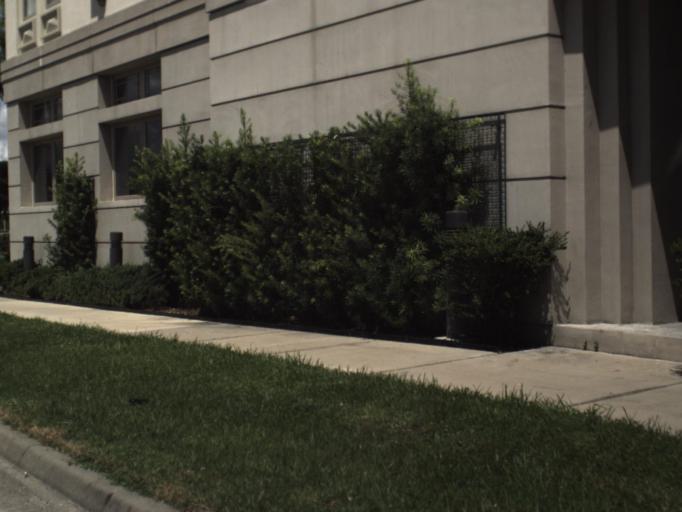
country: US
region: Florida
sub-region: Charlotte County
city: Punta Gorda
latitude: 26.9370
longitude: -82.0508
